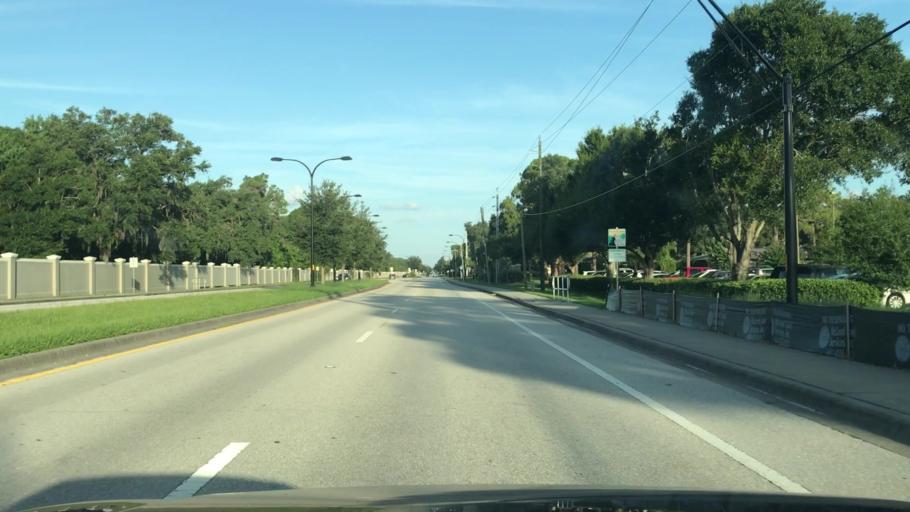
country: US
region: Florida
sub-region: Sarasota County
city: Fruitville
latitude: 27.3232
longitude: -82.4648
